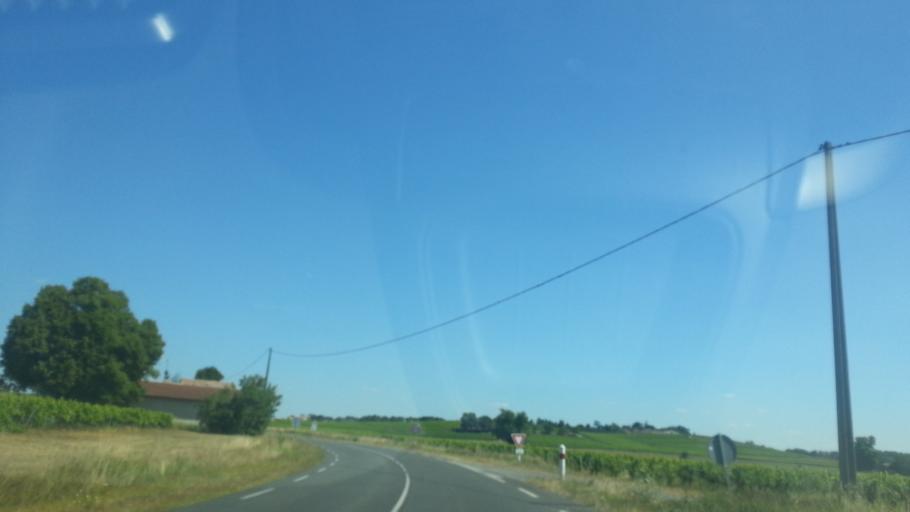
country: FR
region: Aquitaine
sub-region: Departement de la Gironde
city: Illats
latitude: 44.5571
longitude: -0.3529
